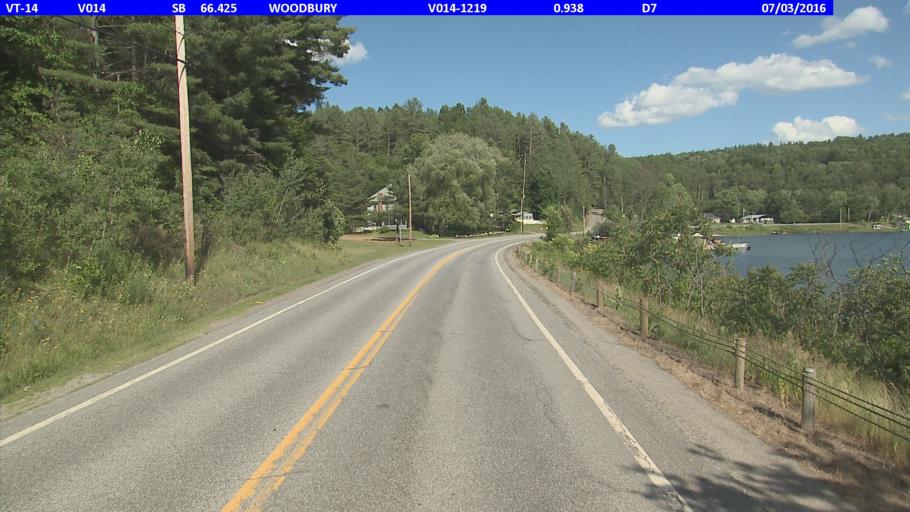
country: US
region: Vermont
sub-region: Caledonia County
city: Hardwick
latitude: 44.4074
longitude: -72.4136
